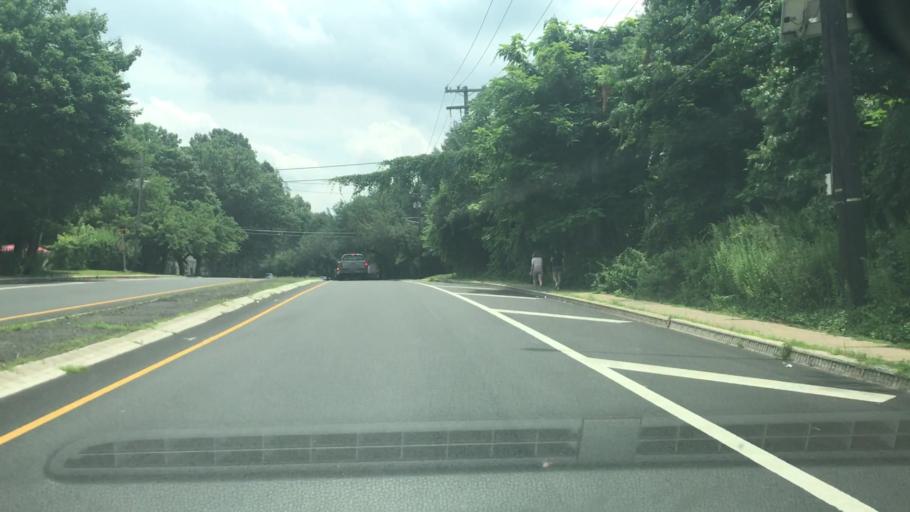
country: US
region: New Jersey
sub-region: Union County
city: Clark
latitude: 40.6401
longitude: -74.3056
